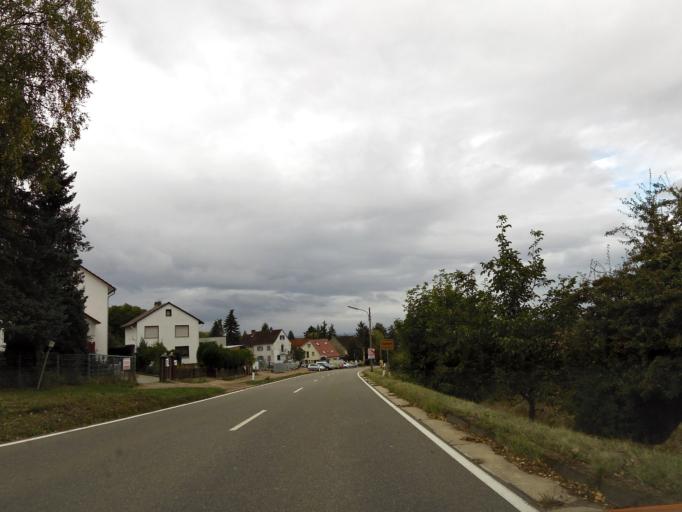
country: DE
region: Rheinland-Pfalz
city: Volxheim
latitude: 49.8155
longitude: 7.9285
